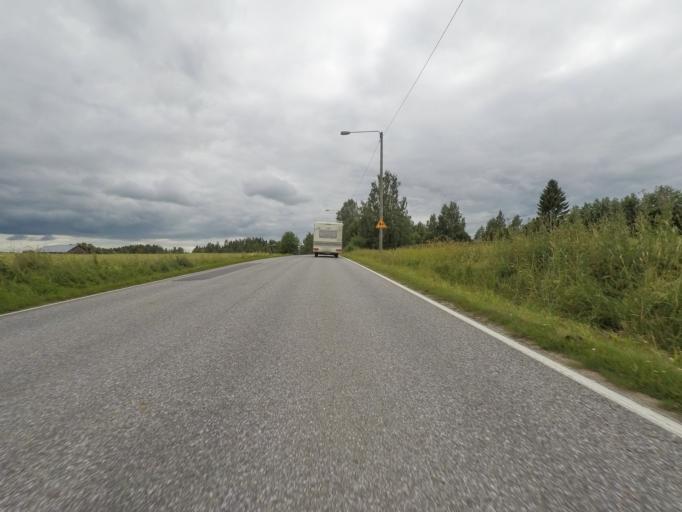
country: FI
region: Varsinais-Suomi
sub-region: Salo
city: Muurla
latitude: 60.3578
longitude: 23.2912
